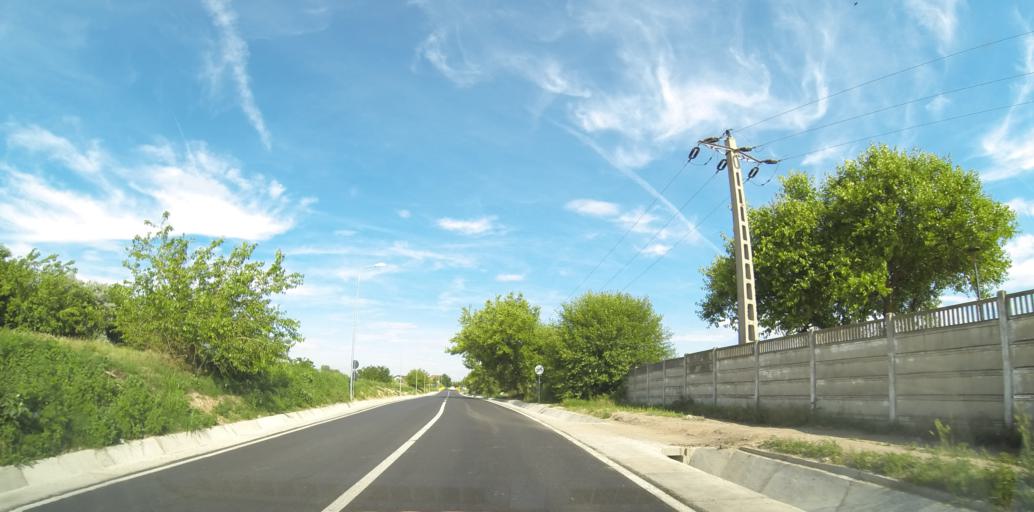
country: RO
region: Dolj
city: Craiova
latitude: 44.3422
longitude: 23.7899
